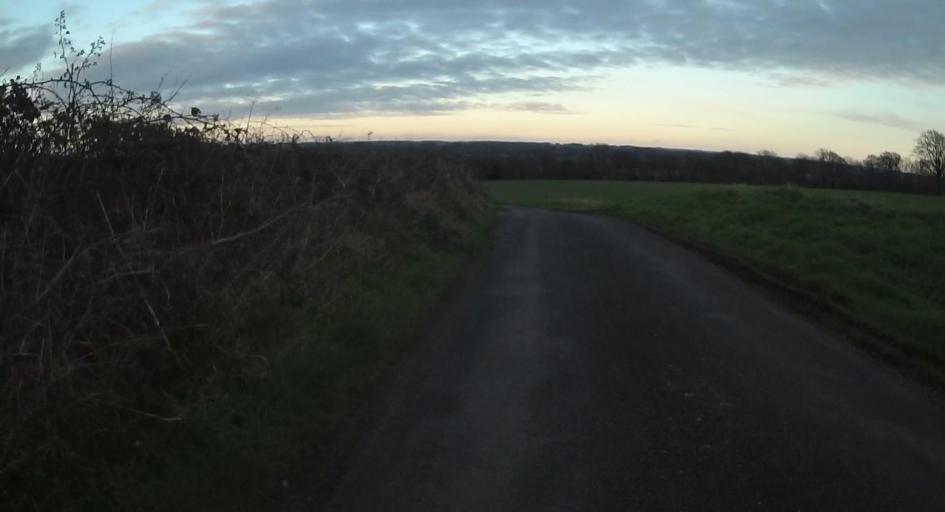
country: GB
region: England
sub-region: Hampshire
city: Swanmore
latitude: 51.0158
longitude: -1.1400
